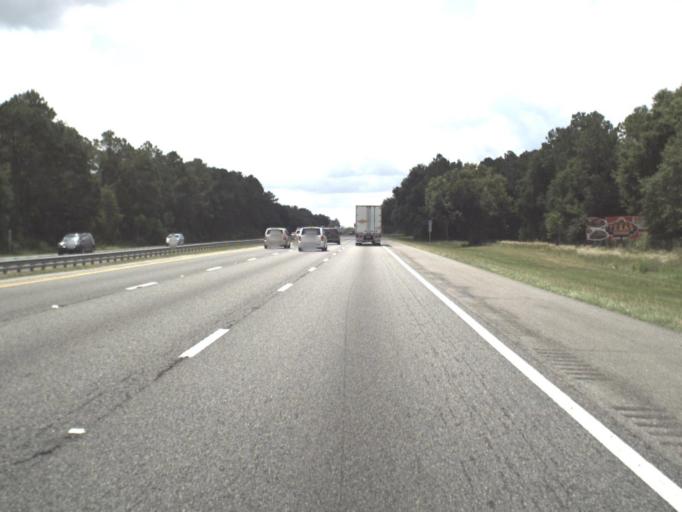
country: US
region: Florida
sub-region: Columbia County
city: Five Points
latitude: 30.2145
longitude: -82.7065
